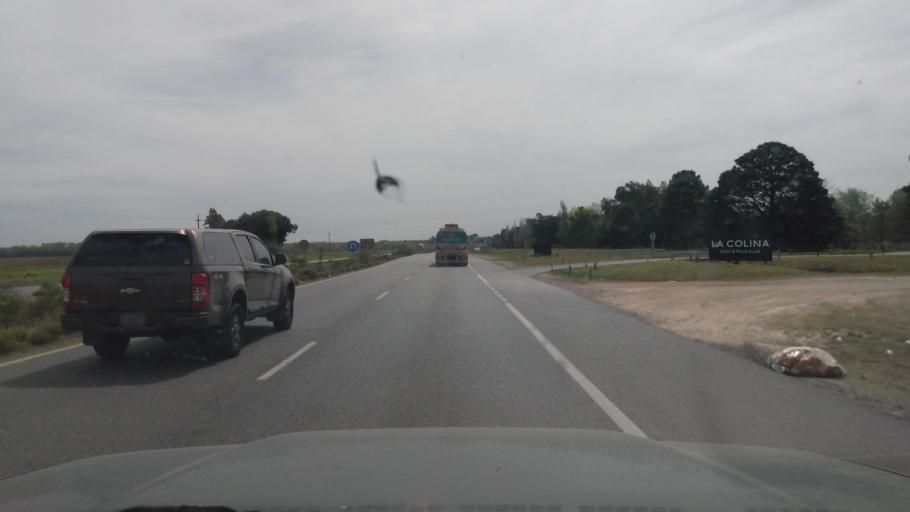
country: AR
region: Buenos Aires
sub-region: Partido de Lujan
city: Lujan
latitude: -34.5315
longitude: -59.0372
